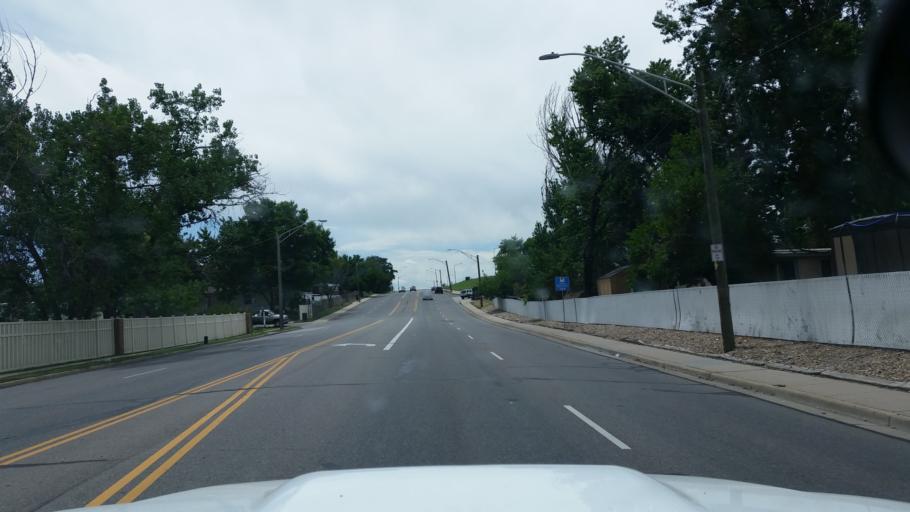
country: US
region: Colorado
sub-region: Adams County
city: Federal Heights
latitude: 39.8612
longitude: -105.0061
